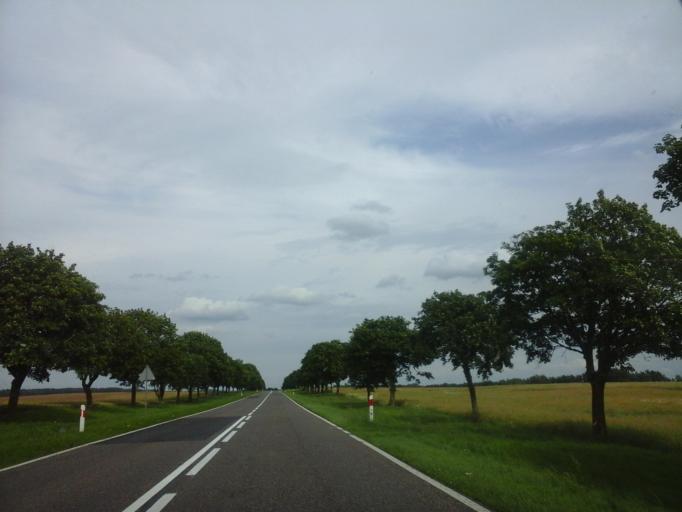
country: PL
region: West Pomeranian Voivodeship
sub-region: Powiat stargardzki
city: Suchan
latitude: 53.2752
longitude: 15.3758
